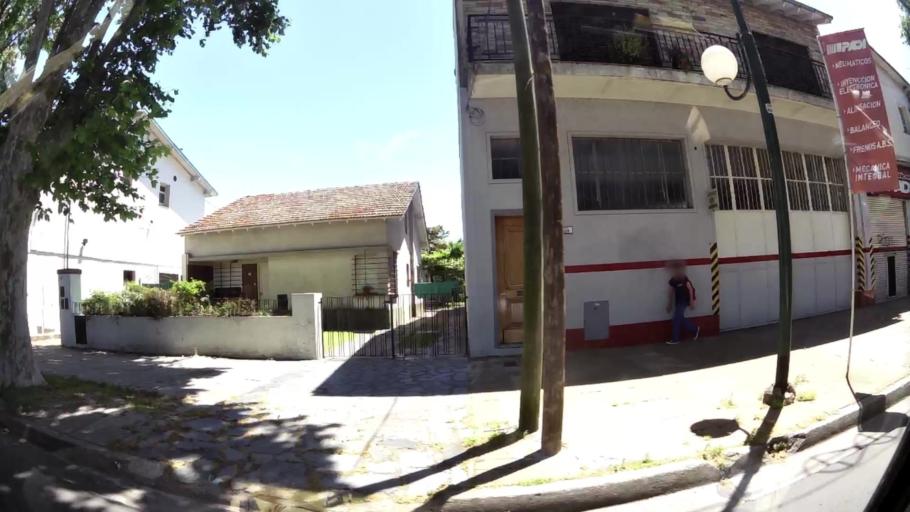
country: AR
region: Buenos Aires
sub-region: Partido de Vicente Lopez
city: Olivos
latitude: -34.4972
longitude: -58.5083
